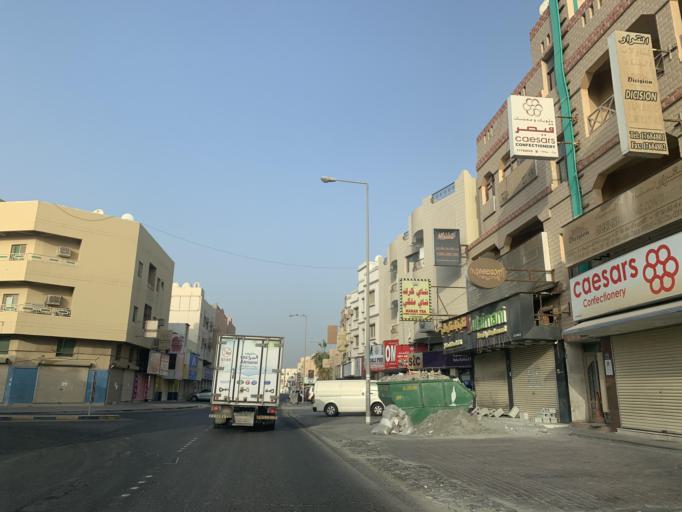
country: BH
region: Northern
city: Madinat `Isa
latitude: 26.1750
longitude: 50.5605
